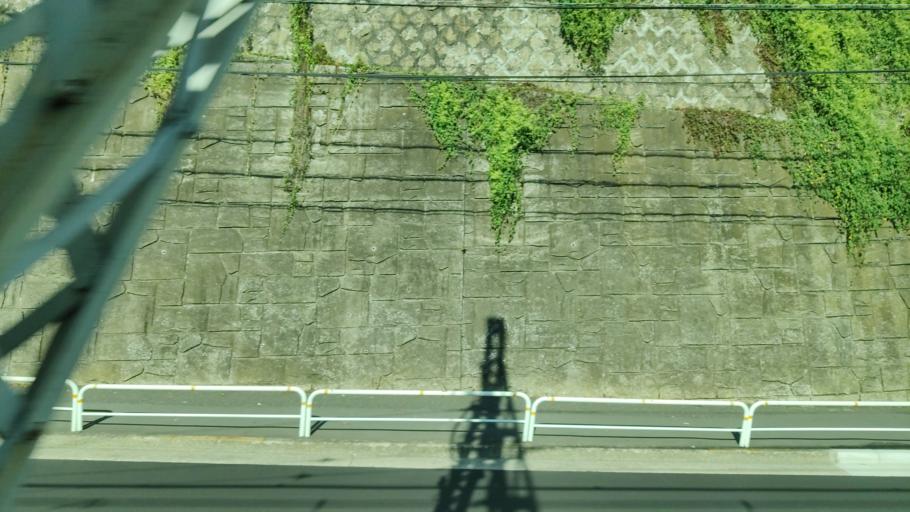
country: JP
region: Tokyo
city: Tokyo
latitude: 35.6299
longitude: 139.7180
